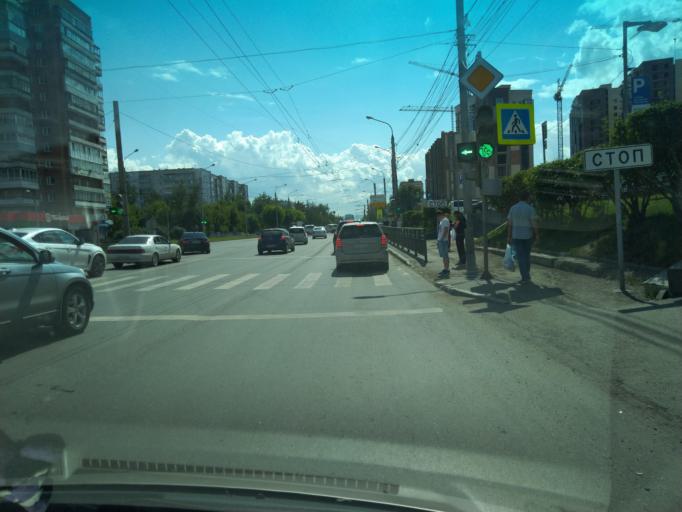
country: RU
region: Krasnoyarskiy
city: Solnechnyy
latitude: 56.0548
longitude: 92.9412
